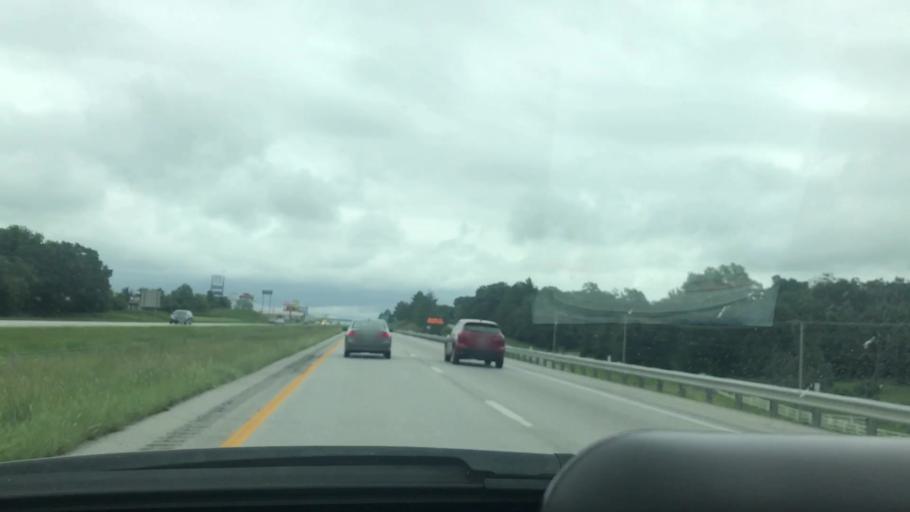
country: US
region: Missouri
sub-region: Jasper County
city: Duquesne
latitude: 37.0508
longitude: -94.4582
